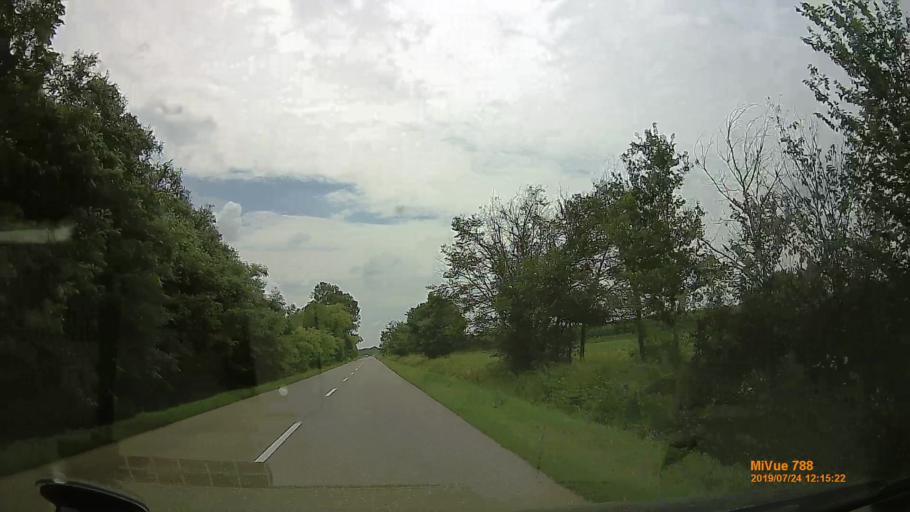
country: HU
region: Szabolcs-Szatmar-Bereg
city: Vasarosnameny
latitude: 48.1851
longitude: 22.3448
